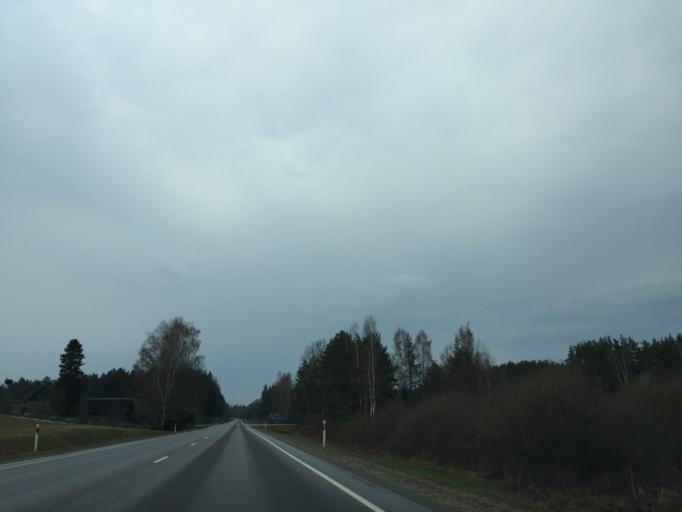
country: EE
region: Tartu
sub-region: UElenurme vald
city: Ulenurme
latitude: 58.1130
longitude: 26.7360
